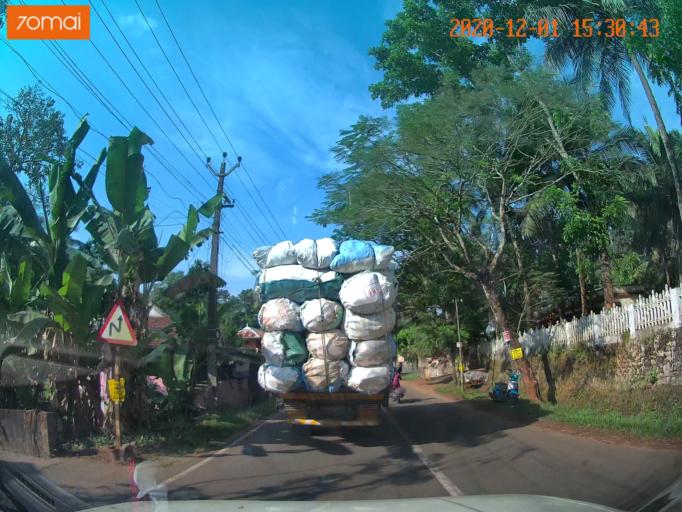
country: IN
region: Kerala
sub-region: Ernakulam
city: Muvattupuzha
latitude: 9.9678
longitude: 76.5662
